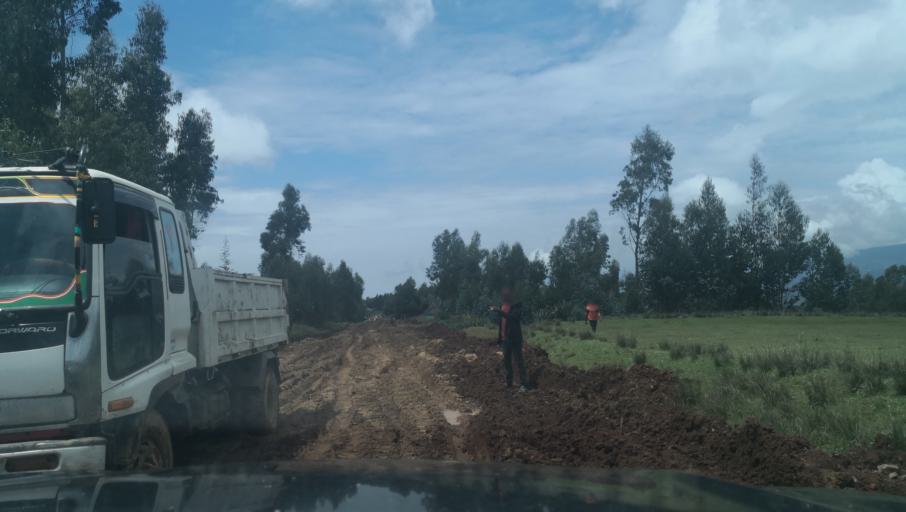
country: ET
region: Southern Nations, Nationalities, and People's Region
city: Butajira
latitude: 8.2913
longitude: 38.4735
